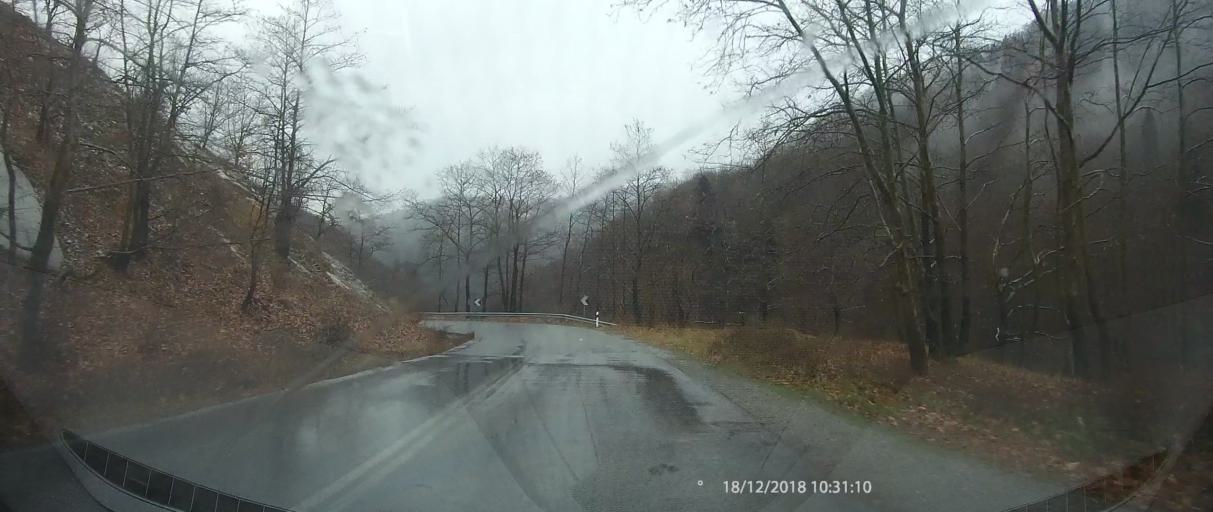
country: GR
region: Central Macedonia
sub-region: Nomos Pierias
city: Kato Milia
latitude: 40.1918
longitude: 22.2825
